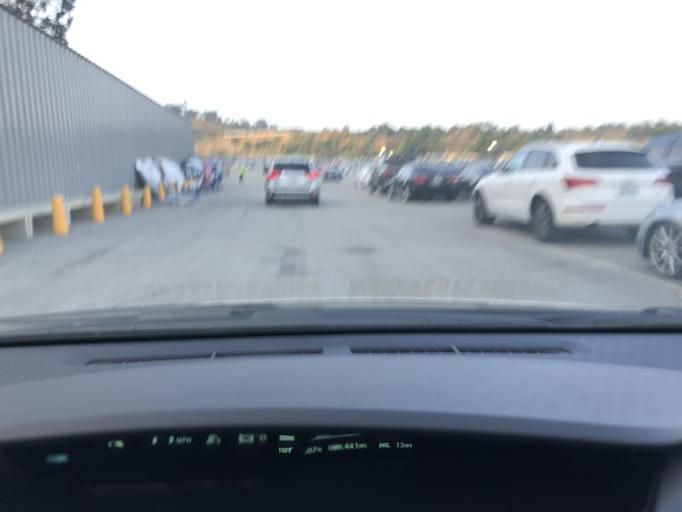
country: US
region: California
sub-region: Los Angeles County
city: Echo Park
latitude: 34.0765
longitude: -118.2442
